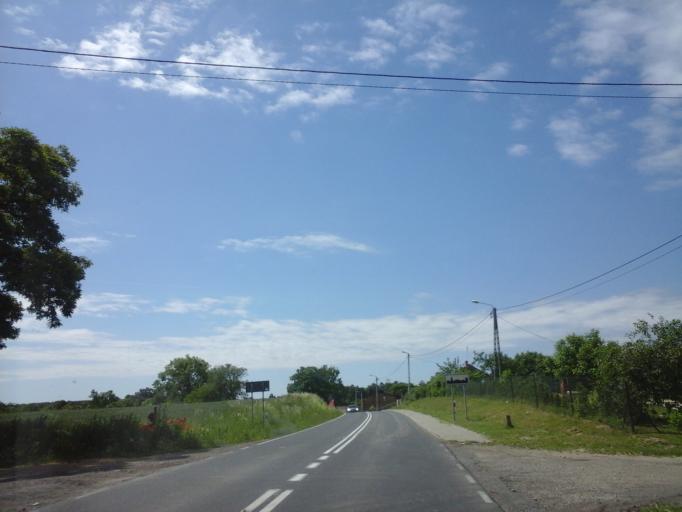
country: PL
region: West Pomeranian Voivodeship
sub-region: Powiat stargardzki
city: Suchan
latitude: 53.2323
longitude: 15.3004
